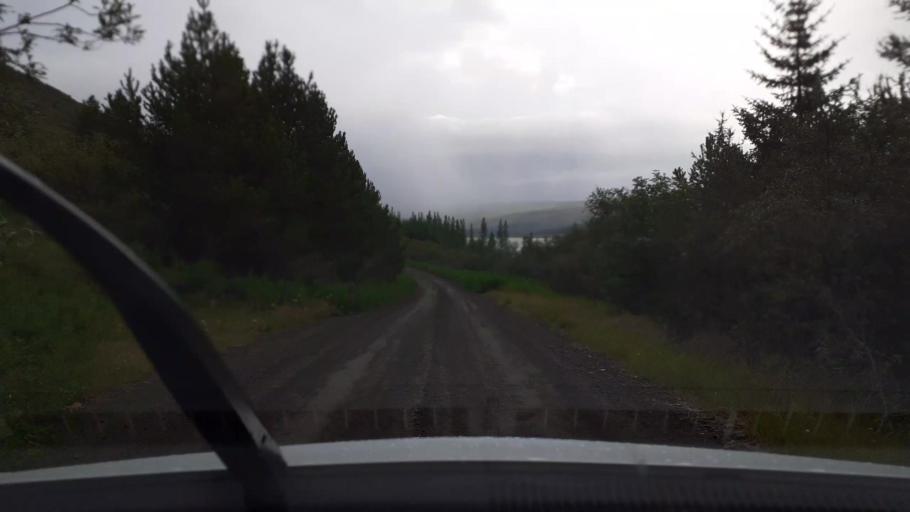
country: IS
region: Capital Region
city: Mosfellsbaer
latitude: 64.4944
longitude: -21.3501
